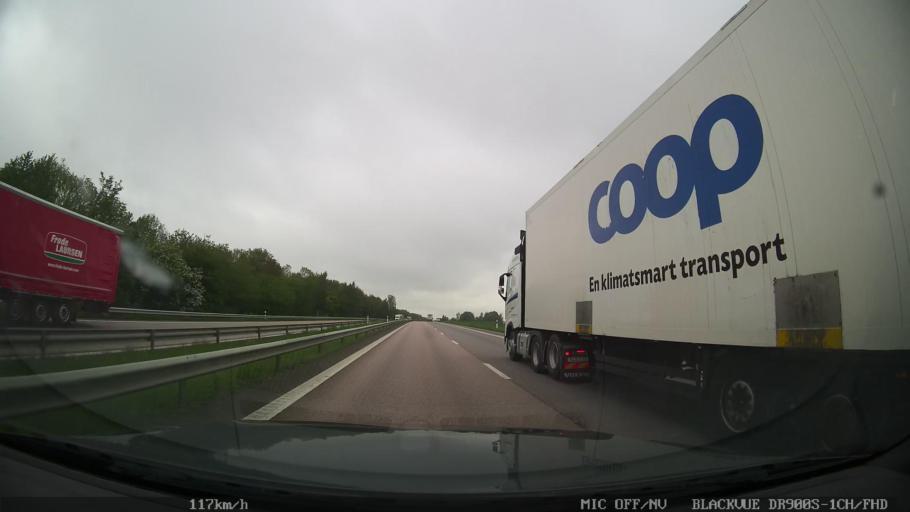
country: SE
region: Skane
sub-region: Helsingborg
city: Gantofta
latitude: 56.0052
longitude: 12.7801
